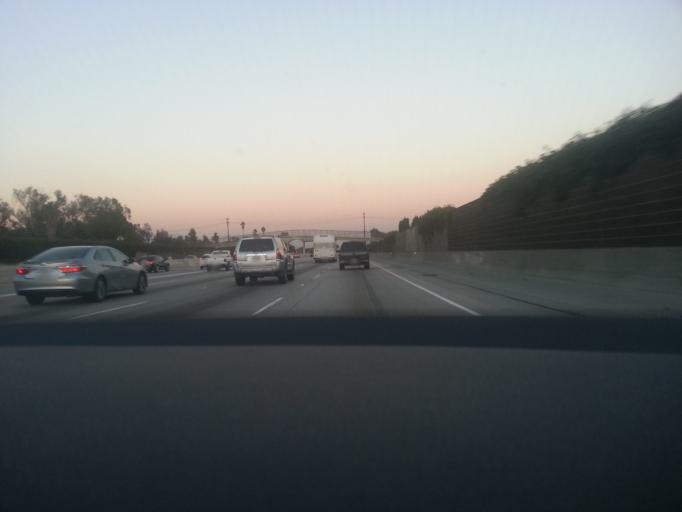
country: US
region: California
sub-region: Los Angeles County
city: Monterey Park
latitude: 34.0712
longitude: -118.1409
